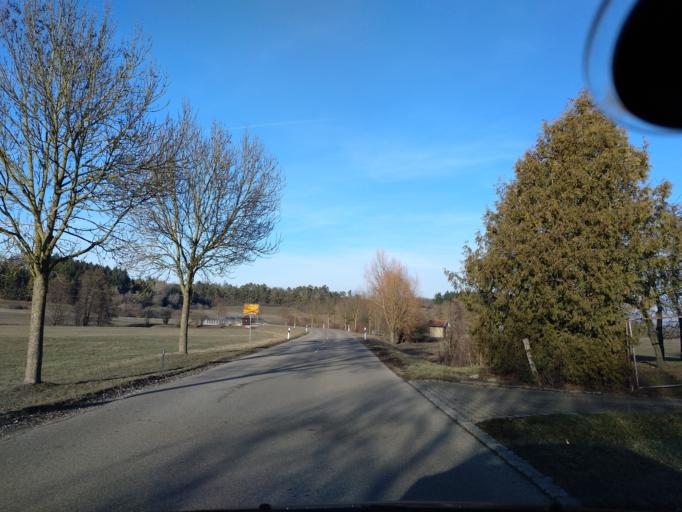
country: DE
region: Baden-Wuerttemberg
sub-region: Regierungsbezirk Stuttgart
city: Crailsheim
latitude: 49.0905
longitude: 10.0229
